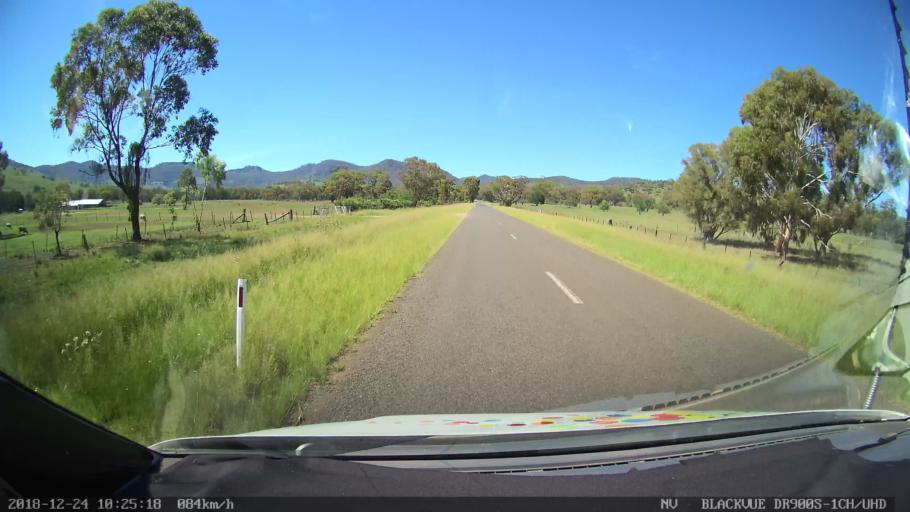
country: AU
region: New South Wales
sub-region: Liverpool Plains
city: Quirindi
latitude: -31.7973
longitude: 150.5290
